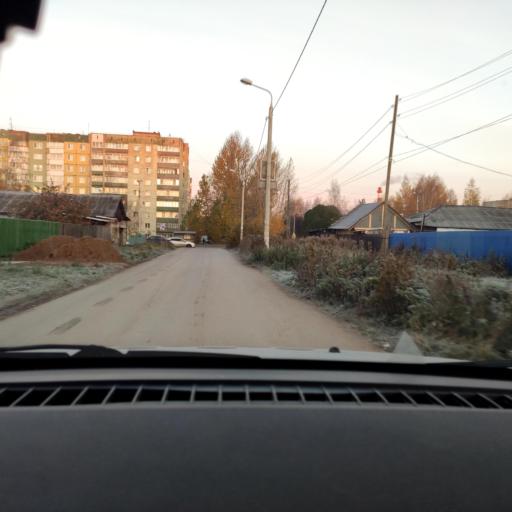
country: RU
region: Perm
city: Perm
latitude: 58.0557
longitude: 56.3578
